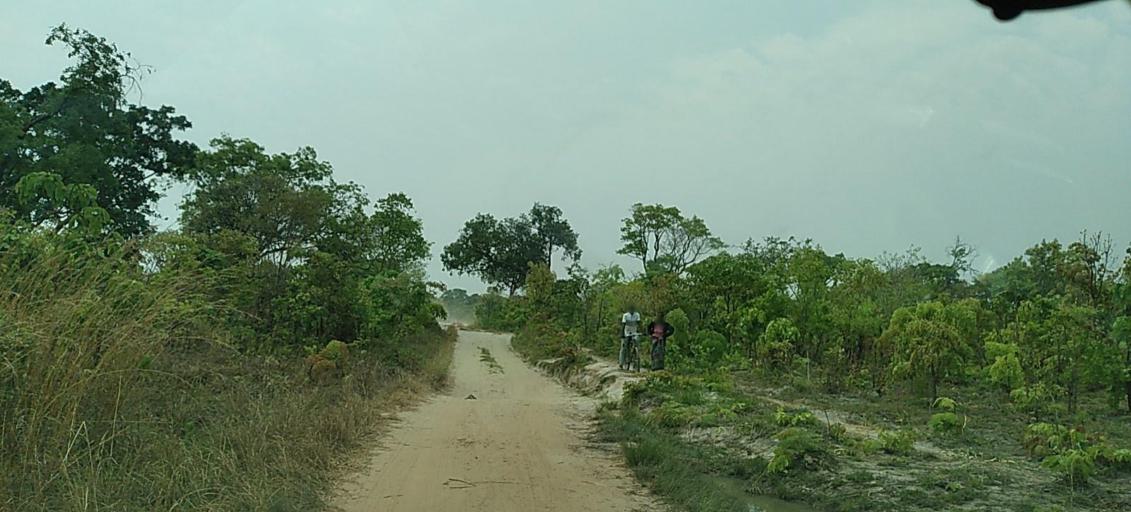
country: ZM
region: North-Western
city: Kabompo
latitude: -13.4754
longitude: 24.4540
